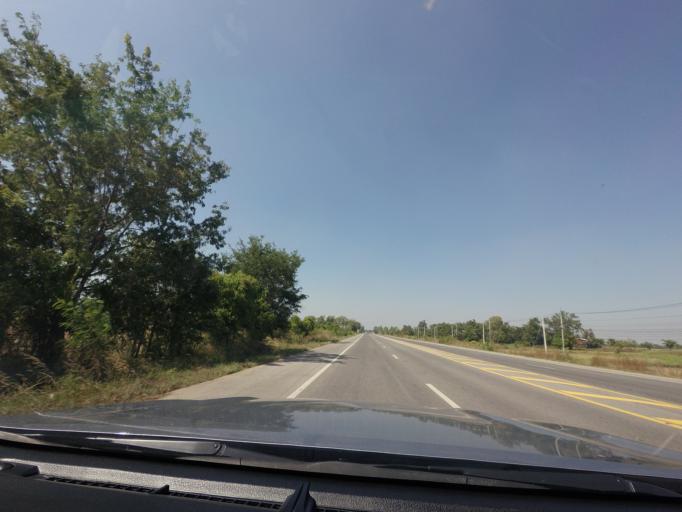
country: TH
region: Sukhothai
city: Ban Na
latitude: 17.0443
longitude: 99.7250
